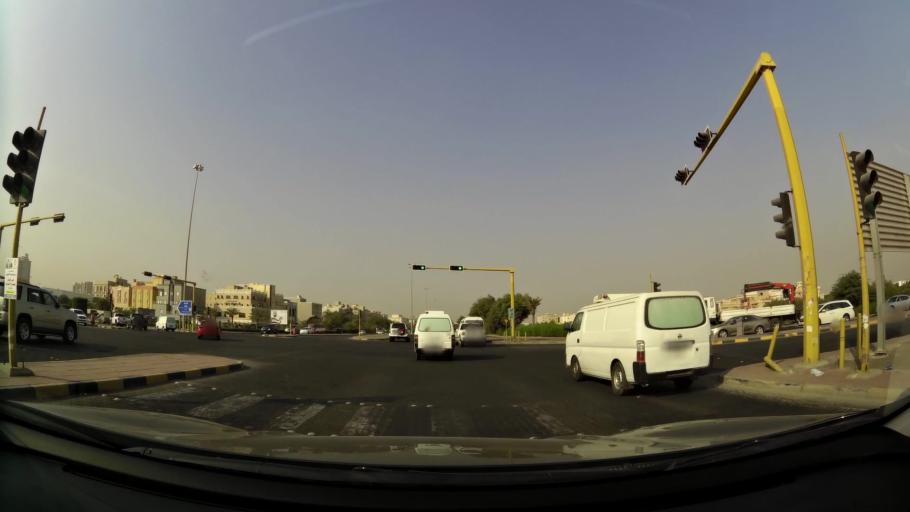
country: KW
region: Mubarak al Kabir
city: Mubarak al Kabir
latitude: 29.1813
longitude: 48.1022
